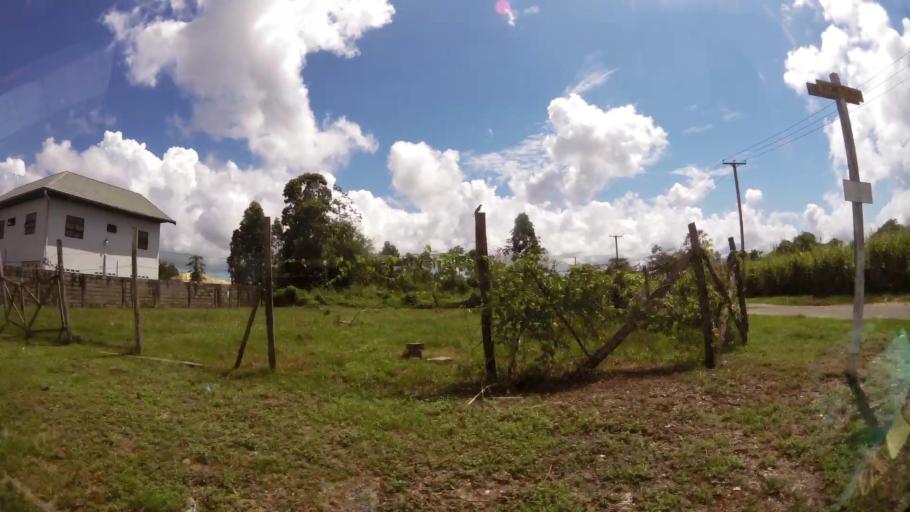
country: SR
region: Paramaribo
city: Paramaribo
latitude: 5.8630
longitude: -55.1326
